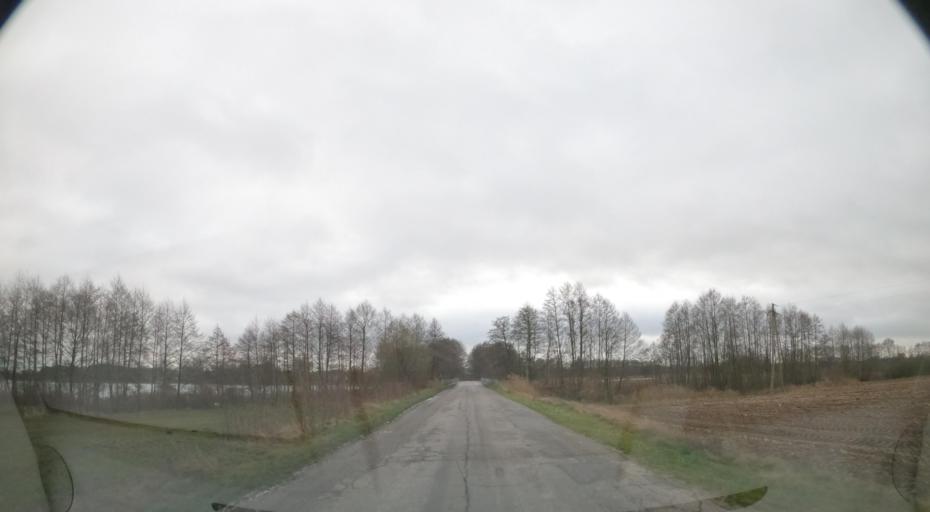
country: PL
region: Greater Poland Voivodeship
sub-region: Powiat pilski
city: Wysoka
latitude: 53.2588
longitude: 17.1166
